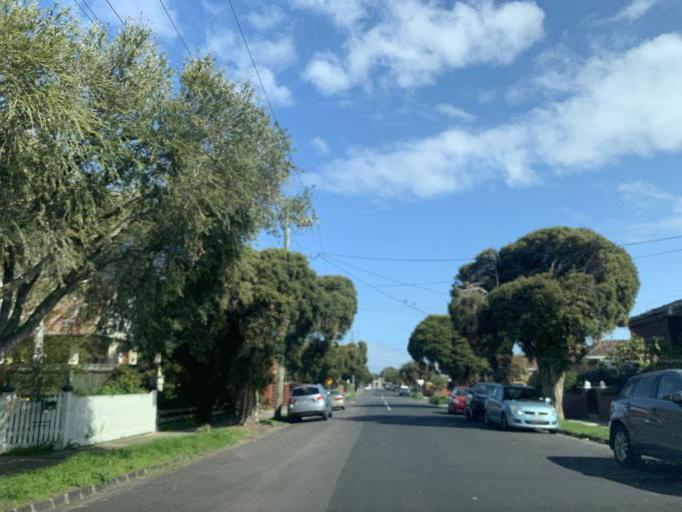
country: AU
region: Victoria
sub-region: Moreland
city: Coburg
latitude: -37.7419
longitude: 144.9613
